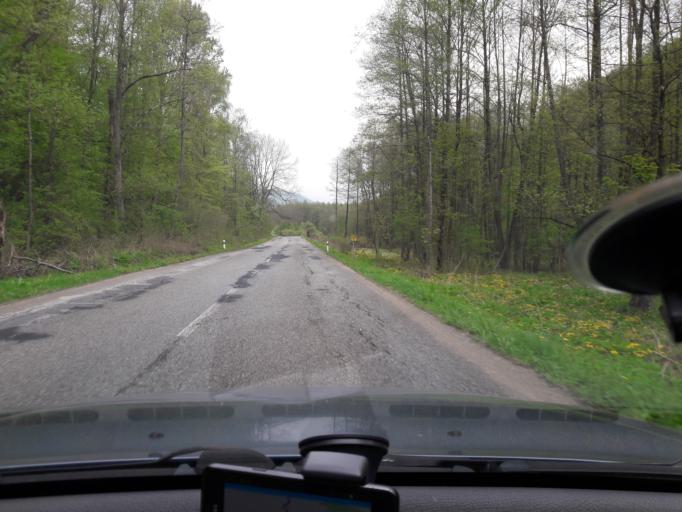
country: SK
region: Banskobystricky
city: Tisovec
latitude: 48.7114
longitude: 19.9996
